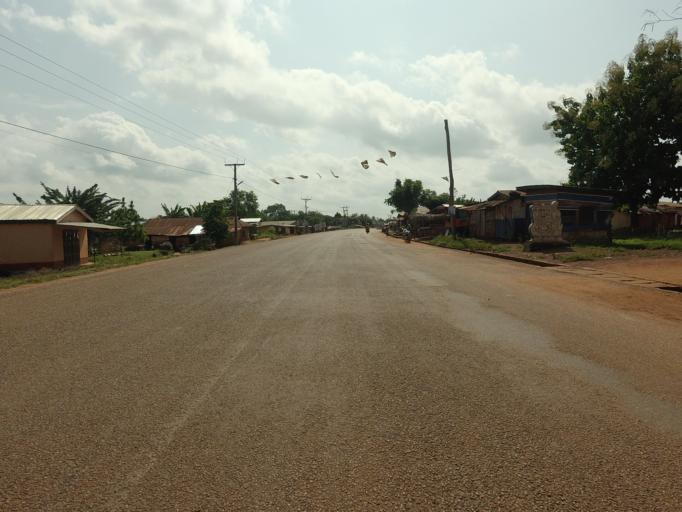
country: TG
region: Maritime
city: Tsevie
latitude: 6.3642
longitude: 0.8540
